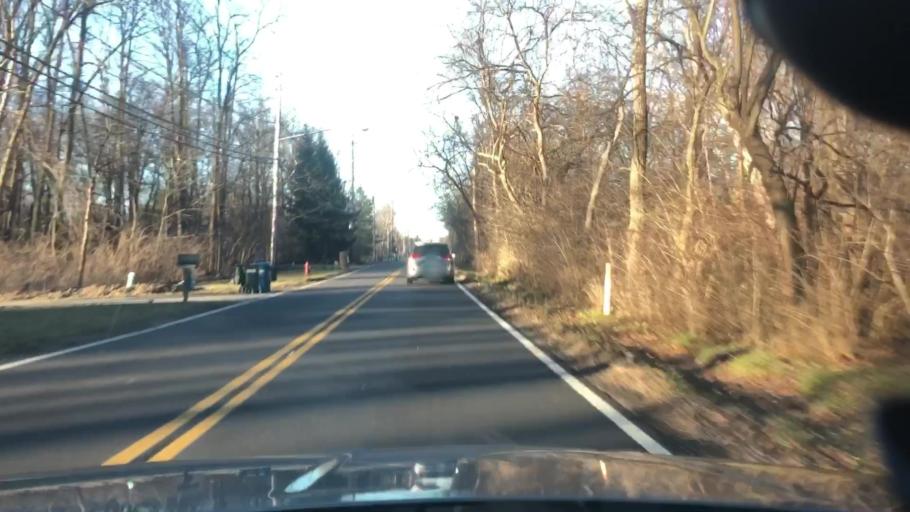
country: US
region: Ohio
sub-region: Cuyahoga County
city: Olmsted Falls
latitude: 41.3690
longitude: -81.8958
